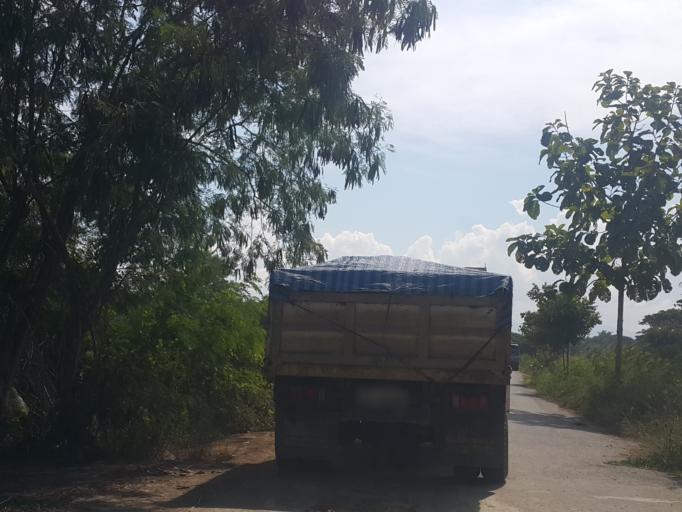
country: TH
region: Chiang Mai
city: San Kamphaeng
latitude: 18.7724
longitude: 99.1046
